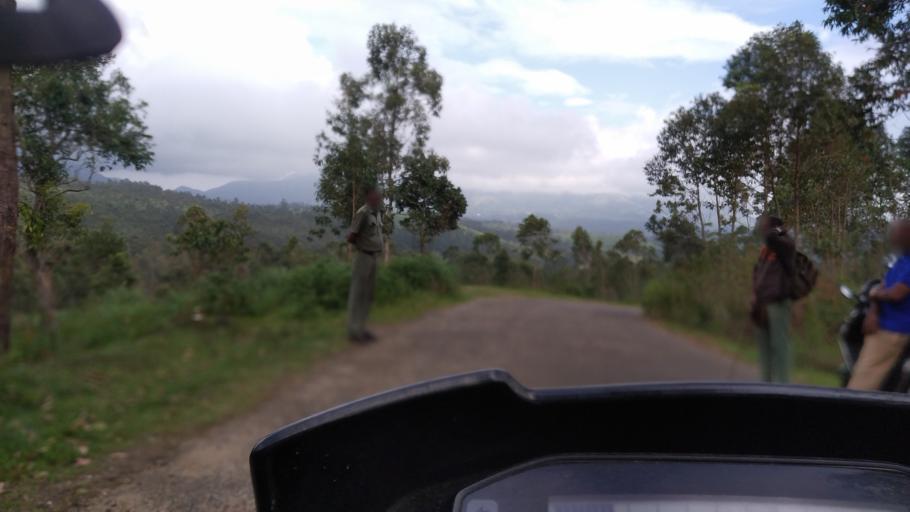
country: IN
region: Kerala
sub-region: Idukki
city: Munnar
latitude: 10.0360
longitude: 77.1890
